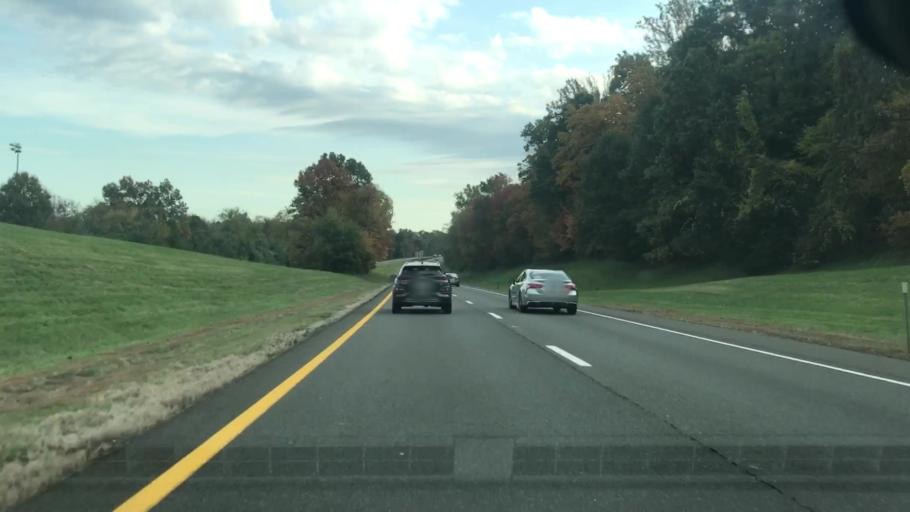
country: US
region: New Jersey
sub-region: Bergen County
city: Woodcliff Lake
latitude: 41.0220
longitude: -74.0697
